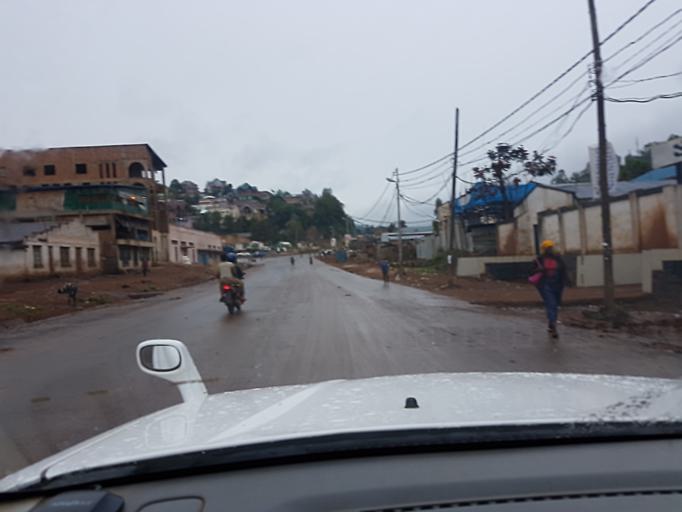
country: CD
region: South Kivu
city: Bukavu
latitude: -2.5014
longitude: 28.8518
